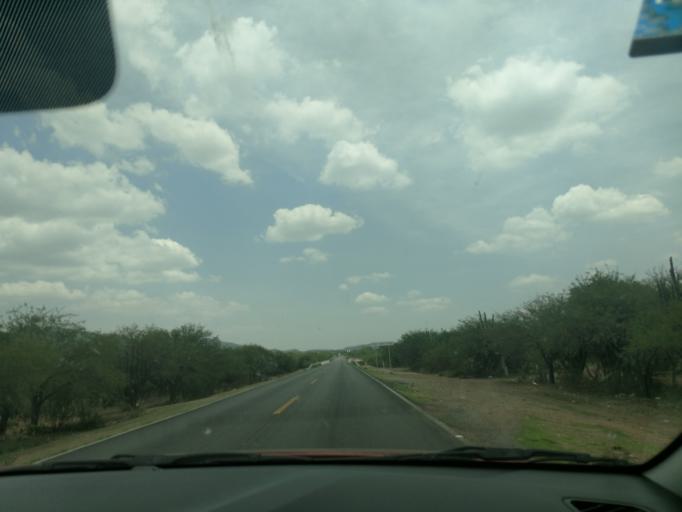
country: MX
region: San Luis Potosi
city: Villa Juarez
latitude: 22.0184
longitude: -100.3955
